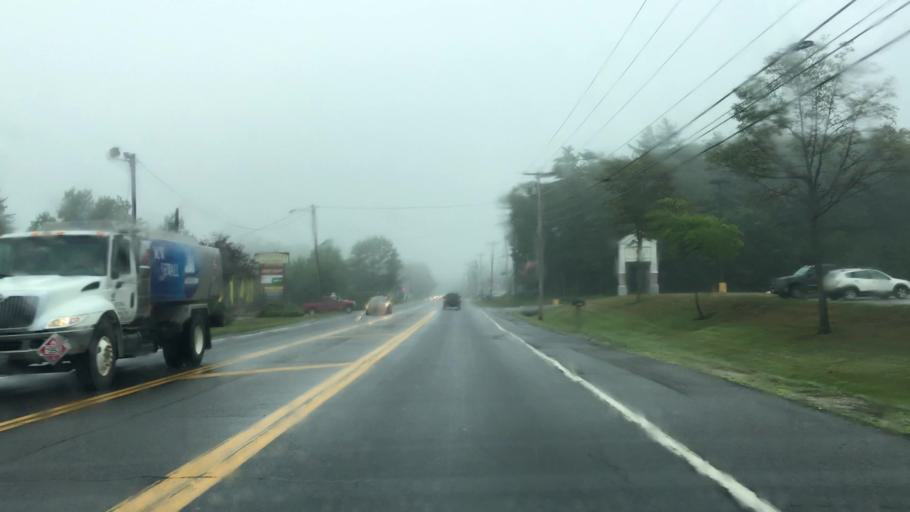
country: US
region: Maine
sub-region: Lincoln County
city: Wiscasset
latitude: 43.9734
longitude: -69.7107
